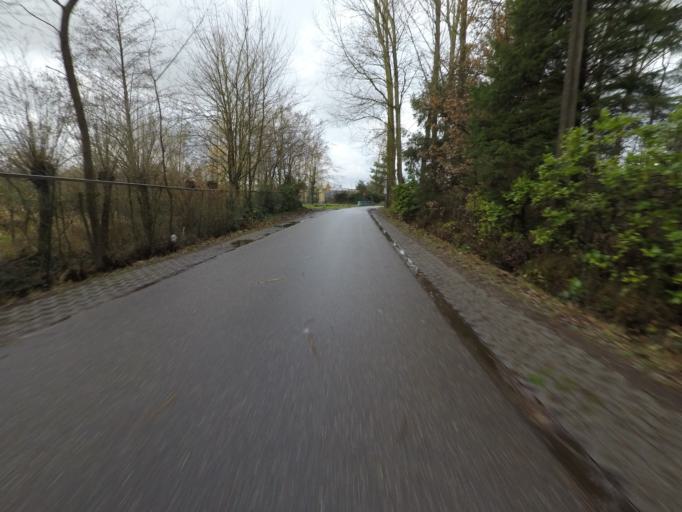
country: BE
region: Flanders
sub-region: Provincie Vlaams-Brabant
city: Begijnendijk
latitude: 51.0228
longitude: 4.7585
